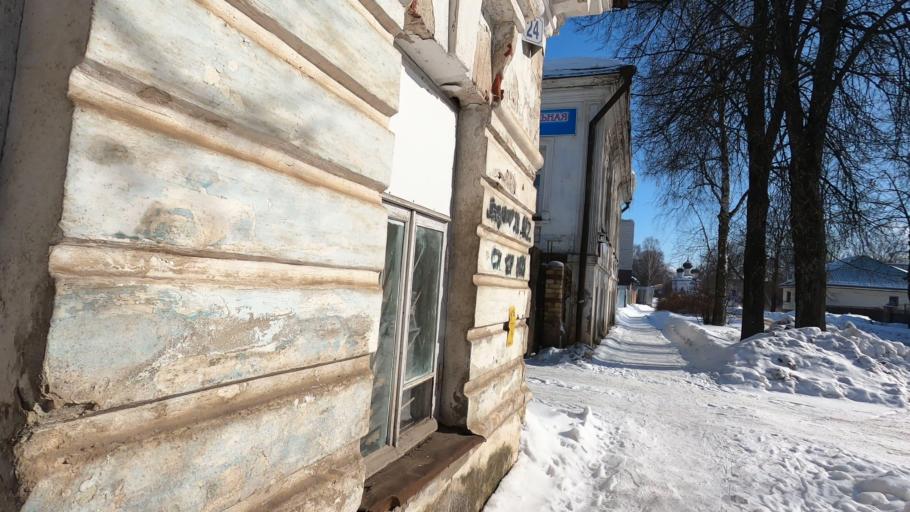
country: RU
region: Jaroslavl
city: Rybinsk
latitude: 58.0459
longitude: 38.8655
